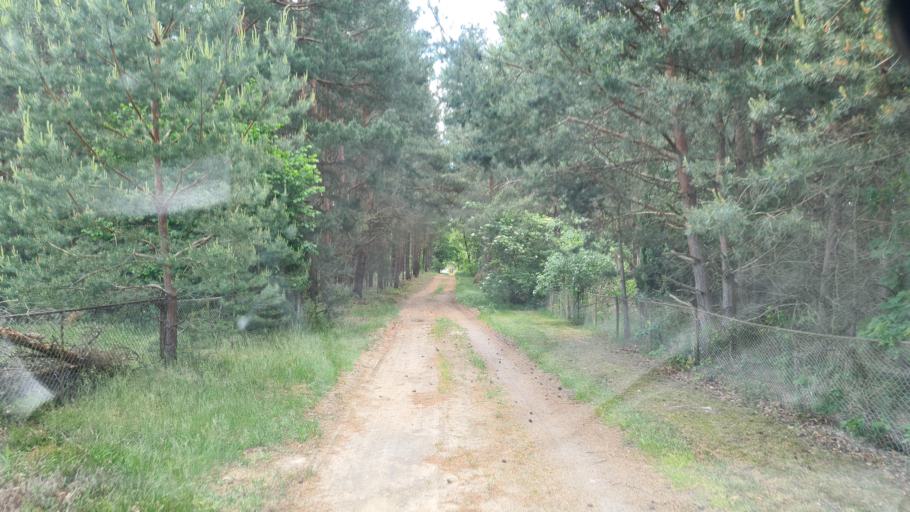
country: DE
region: Brandenburg
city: Finsterwalde
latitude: 51.6456
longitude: 13.7871
